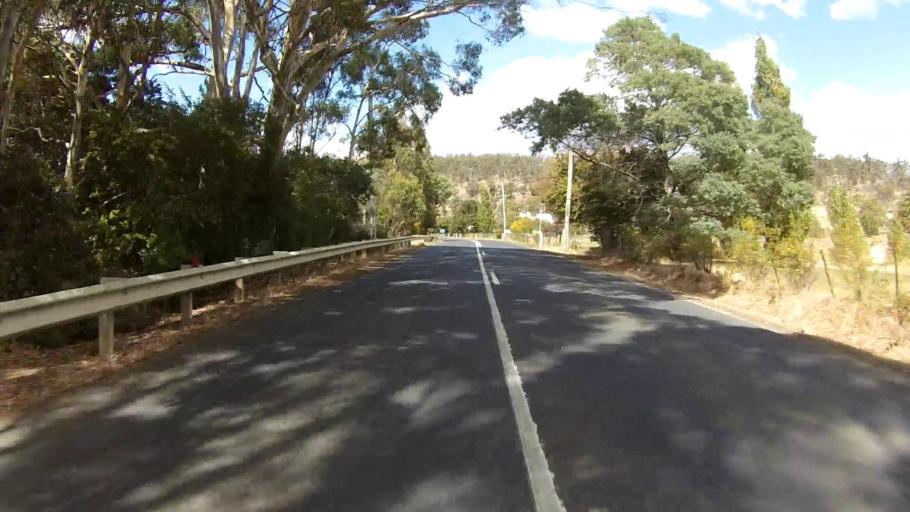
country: AU
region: Tasmania
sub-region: Derwent Valley
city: New Norfolk
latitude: -42.7742
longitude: 147.0276
